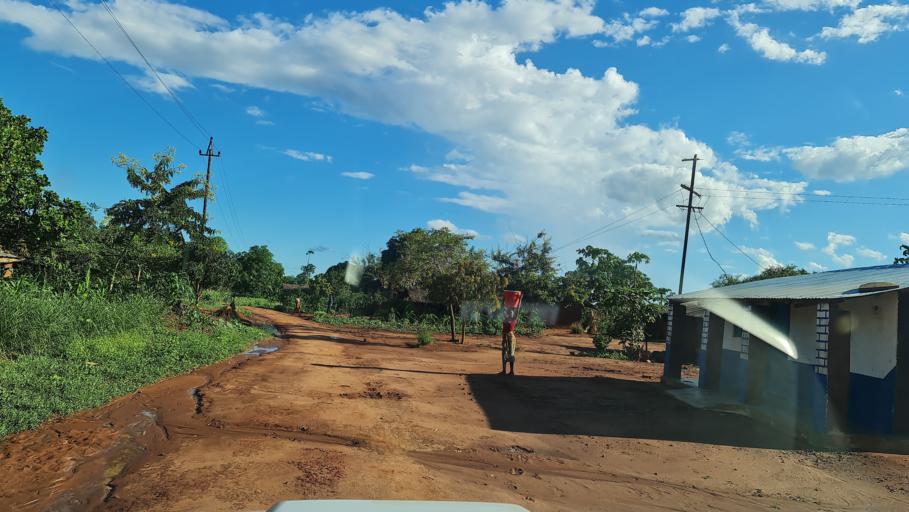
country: MZ
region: Nampula
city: Ilha de Mocambique
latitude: -14.9184
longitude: 40.2172
